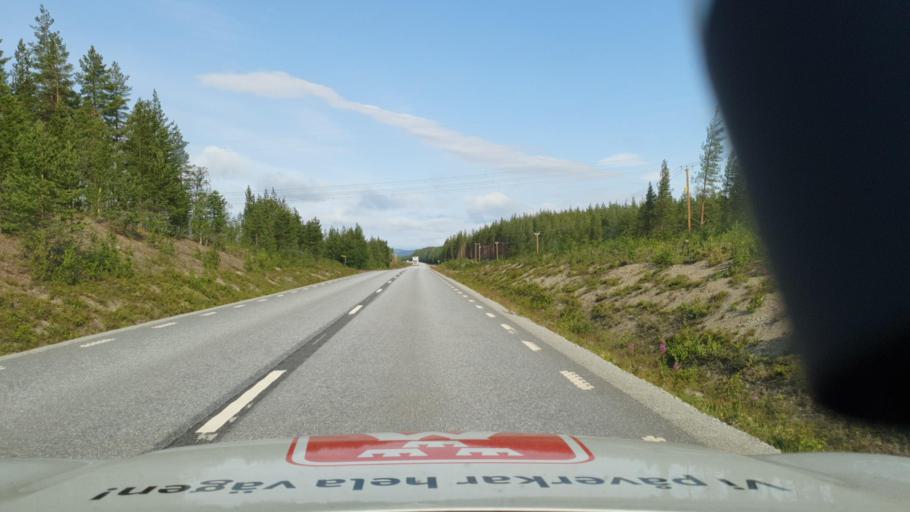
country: SE
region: Vaesternorrland
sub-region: OErnskoeldsviks Kommun
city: Bredbyn
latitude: 64.0952
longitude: 18.1796
